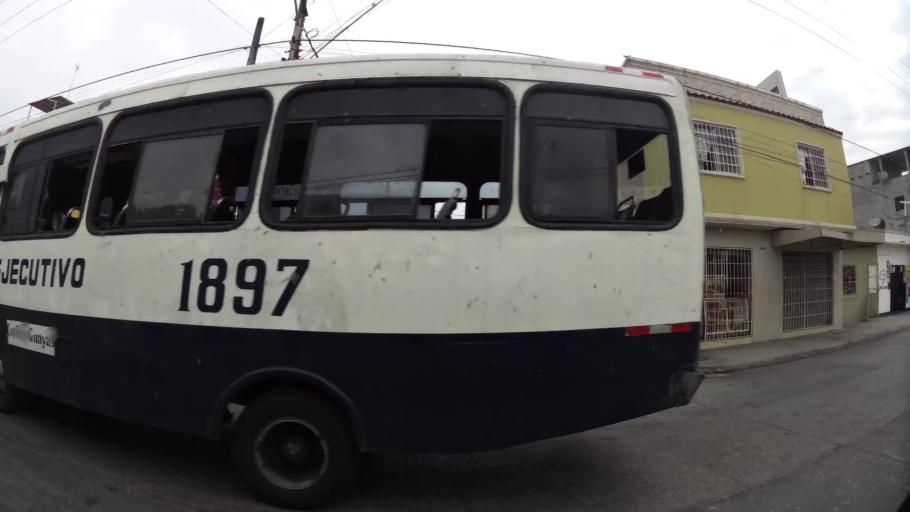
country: EC
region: Guayas
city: Guayaquil
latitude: -2.2555
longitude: -79.8721
